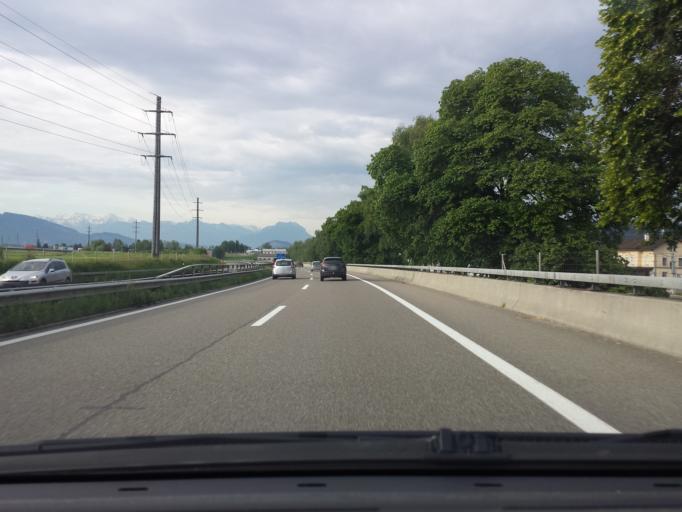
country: CH
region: Saint Gallen
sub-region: Wahlkreis Rheintal
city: Au
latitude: 47.4374
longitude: 9.6428
